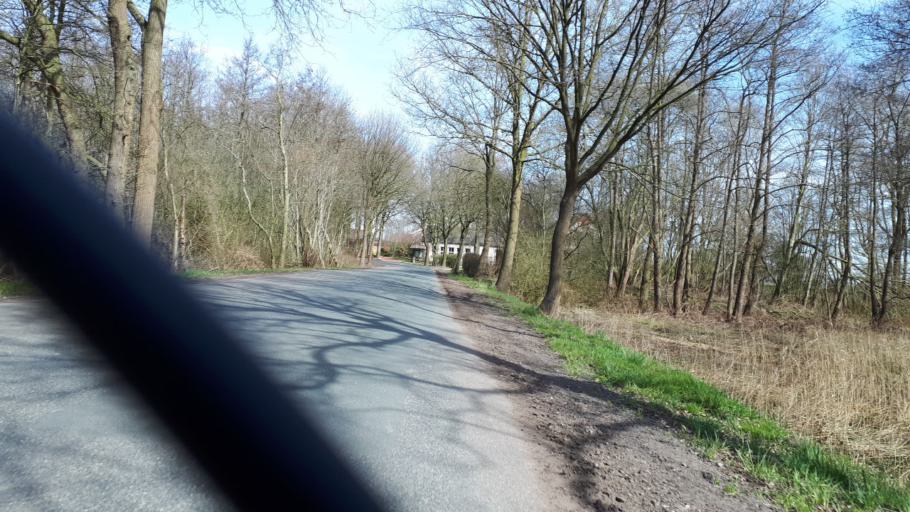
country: DE
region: Lower Saxony
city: Cloppenburg
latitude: 52.8524
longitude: 7.9942
